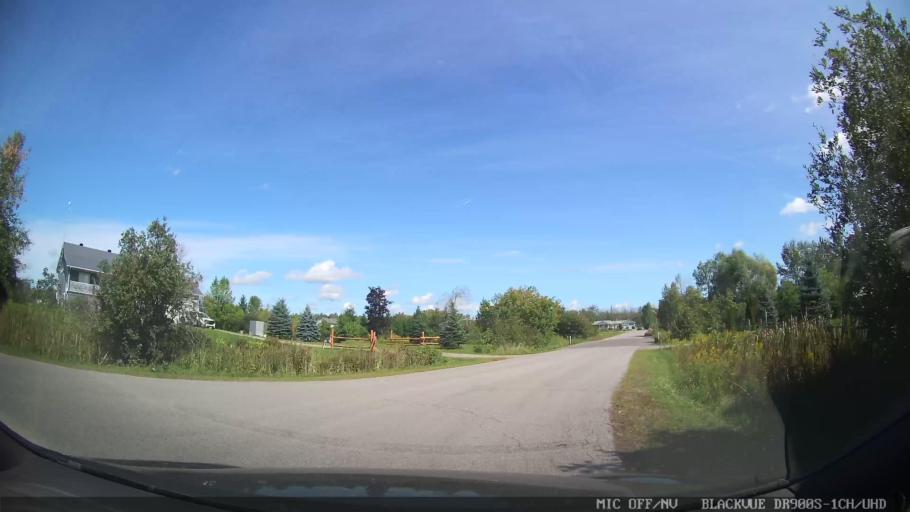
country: CA
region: Ontario
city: Bells Corners
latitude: 45.0660
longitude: -75.6660
